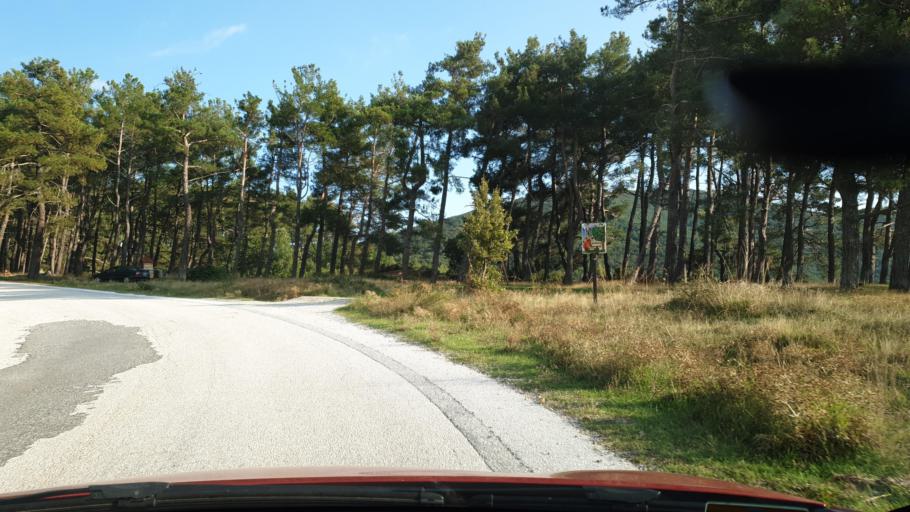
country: GR
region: Central Macedonia
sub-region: Nomos Thessalonikis
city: Peristera
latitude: 40.5135
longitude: 23.2145
